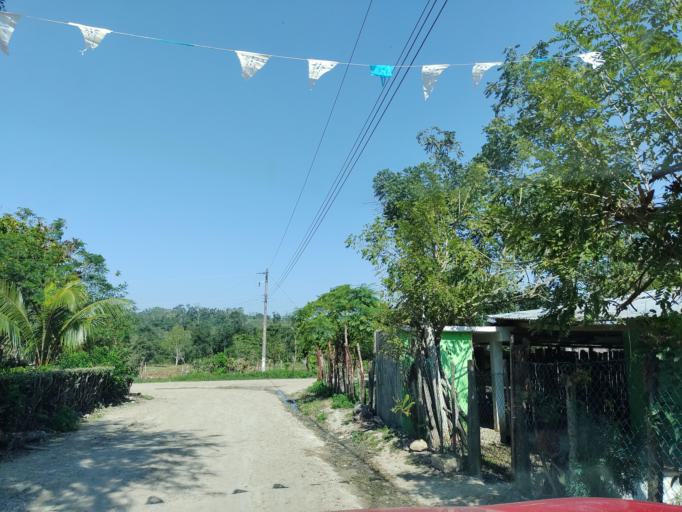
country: MX
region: Veracruz
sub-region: Papantla
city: Polutla
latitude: 20.5189
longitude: -97.2445
